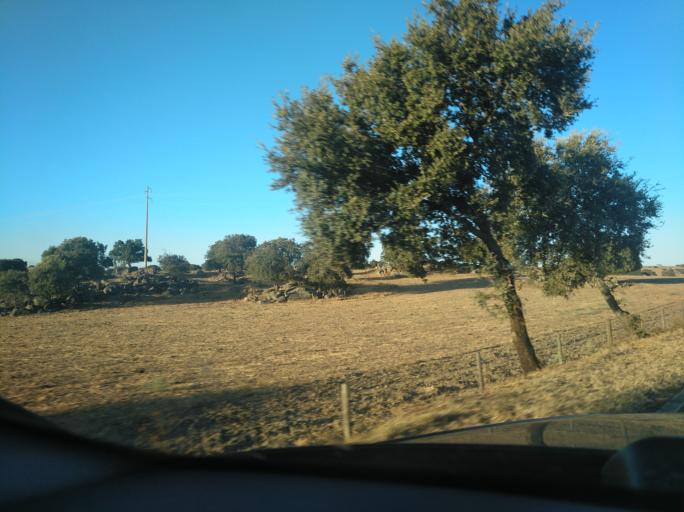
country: PT
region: Portalegre
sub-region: Arronches
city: Arronches
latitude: 39.0684
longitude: -7.2103
